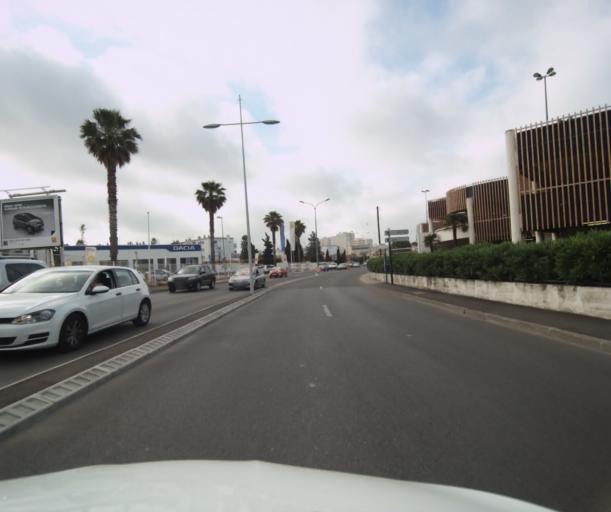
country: FR
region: Provence-Alpes-Cote d'Azur
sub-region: Departement du Var
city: Six-Fours-les-Plages
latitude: 43.1130
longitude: 5.8584
